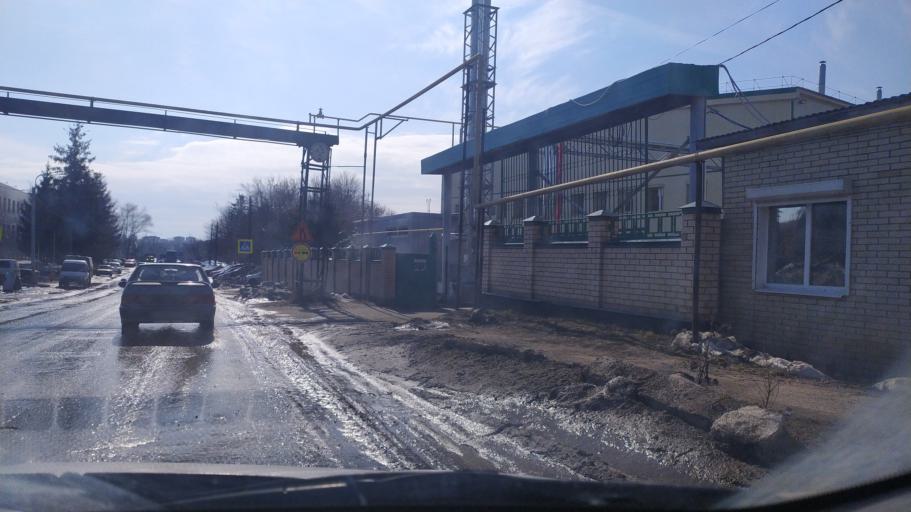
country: RU
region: Chuvashia
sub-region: Cheboksarskiy Rayon
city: Cheboksary
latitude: 56.1192
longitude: 47.2901
